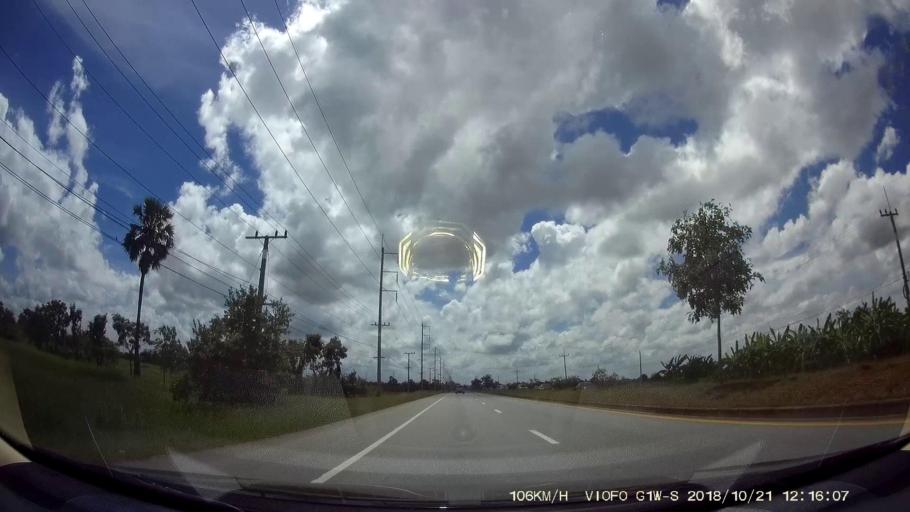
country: TH
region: Nakhon Ratchasima
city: Dan Khun Thot
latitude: 15.3522
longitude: 101.8272
